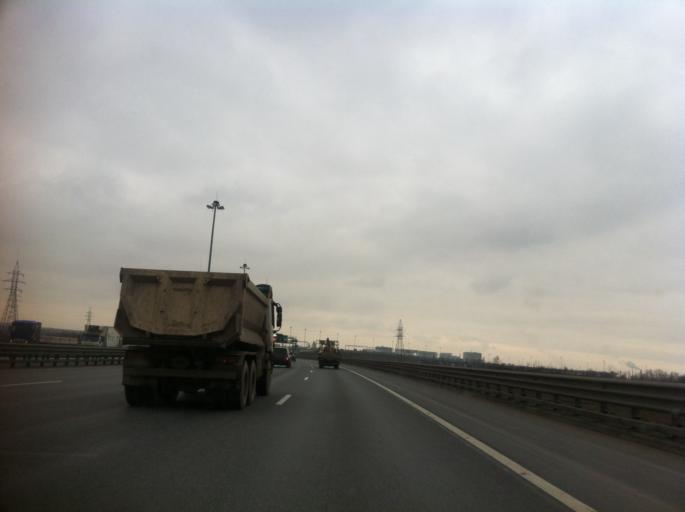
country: RU
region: St.-Petersburg
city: Shushary
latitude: 59.8138
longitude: 30.3485
